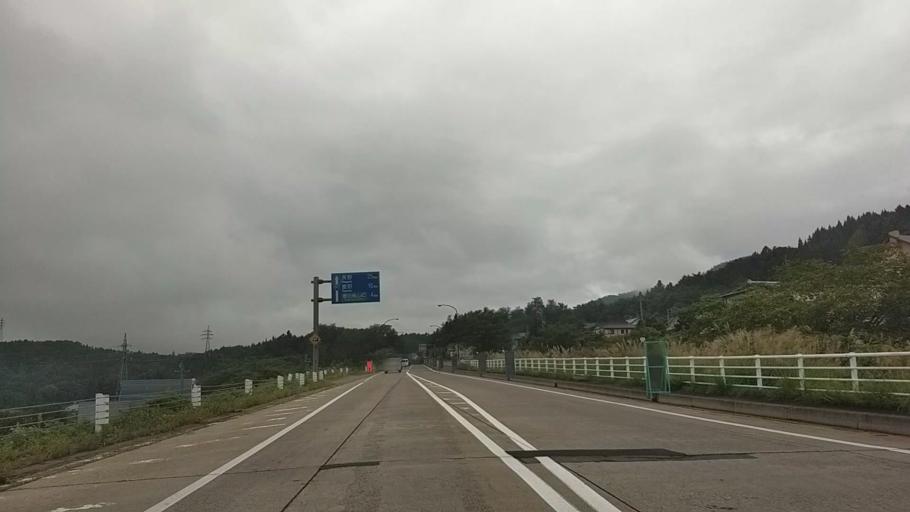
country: JP
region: Nagano
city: Iiyama
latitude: 36.8228
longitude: 138.3499
